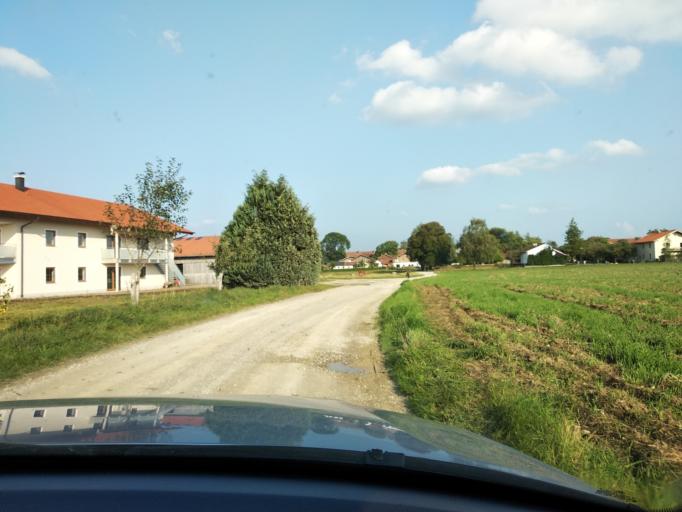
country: DE
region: Bavaria
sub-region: Upper Bavaria
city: Obing
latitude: 47.9945
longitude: 12.4245
